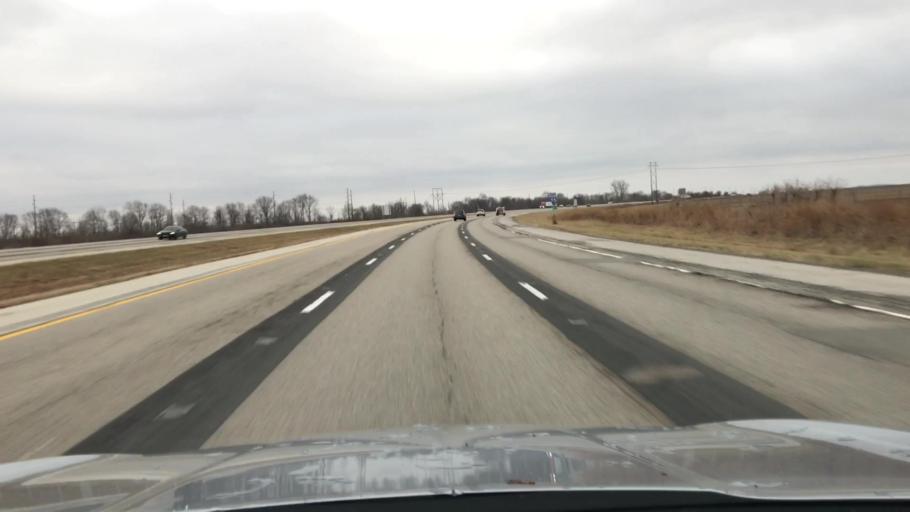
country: US
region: Illinois
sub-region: Logan County
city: Lincoln
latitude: 40.1046
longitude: -89.4165
